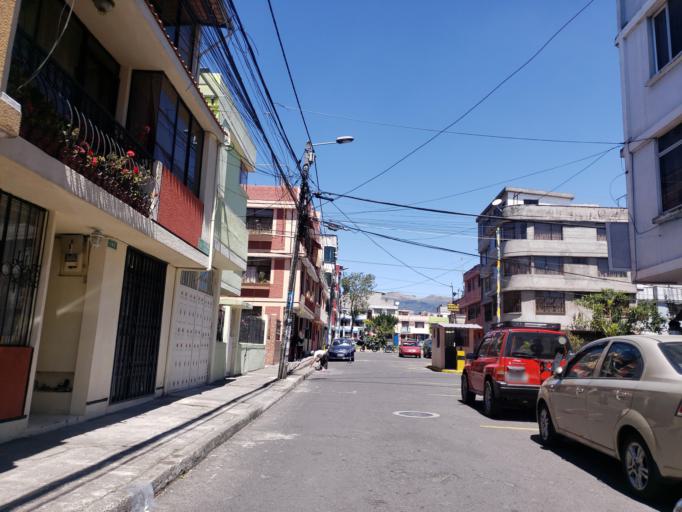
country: EC
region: Pichincha
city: Quito
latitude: -0.2683
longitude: -78.5364
